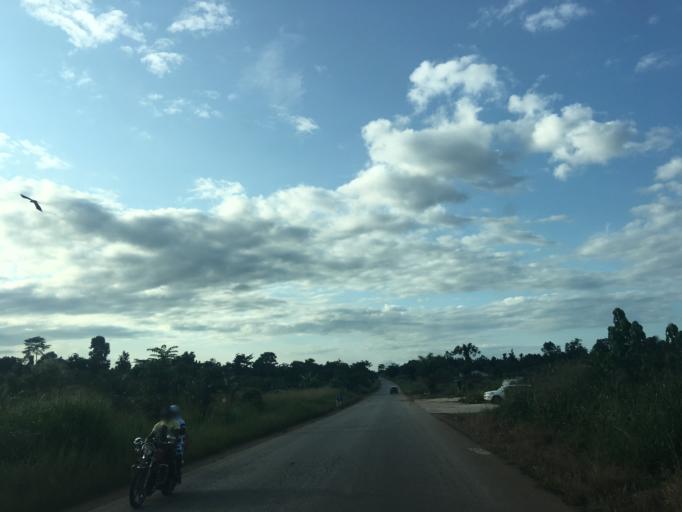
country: GH
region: Western
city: Bibiani
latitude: 6.3090
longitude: -2.2506
